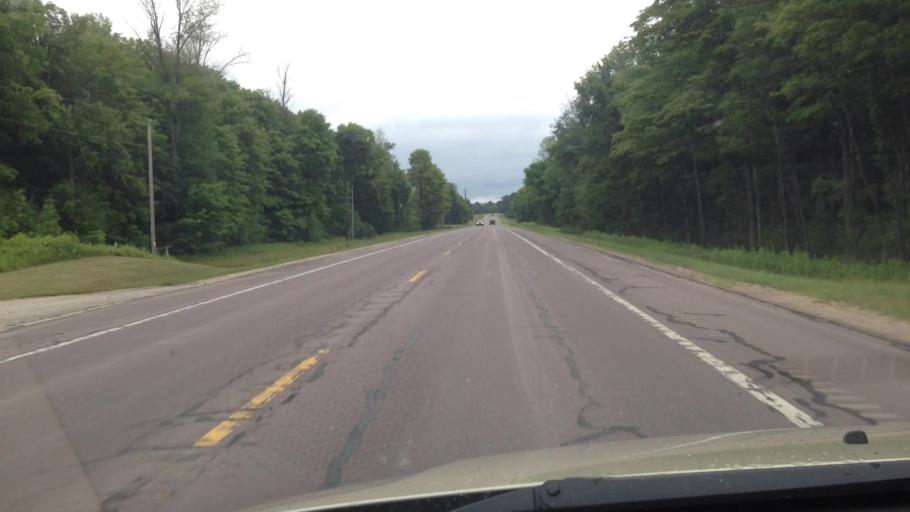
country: US
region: Michigan
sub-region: Schoolcraft County
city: Manistique
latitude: 46.0864
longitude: -85.9543
